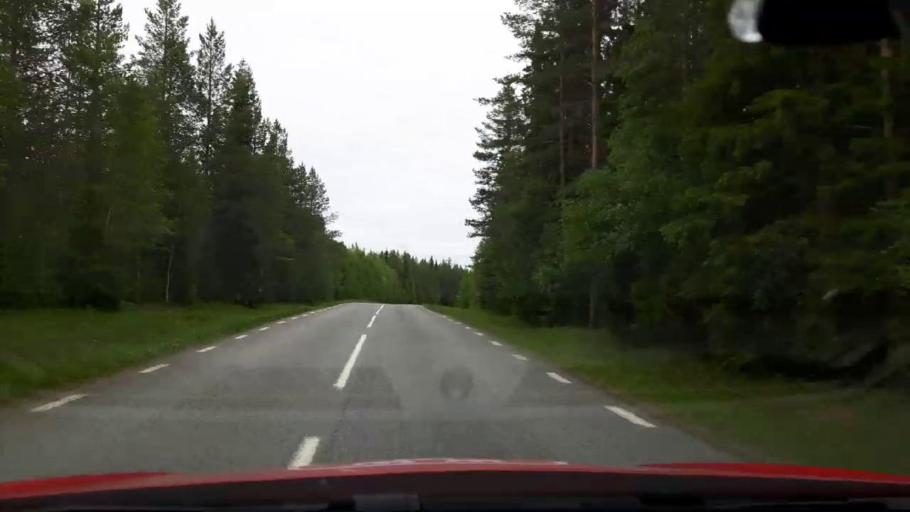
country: SE
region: Jaemtland
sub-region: Stroemsunds Kommun
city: Stroemsund
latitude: 63.4532
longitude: 15.4643
